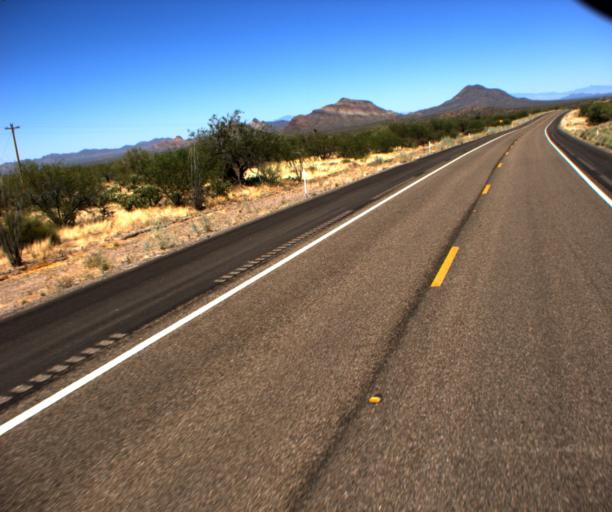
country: US
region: Arizona
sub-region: Pima County
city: Three Points
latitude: 32.0358
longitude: -111.5418
